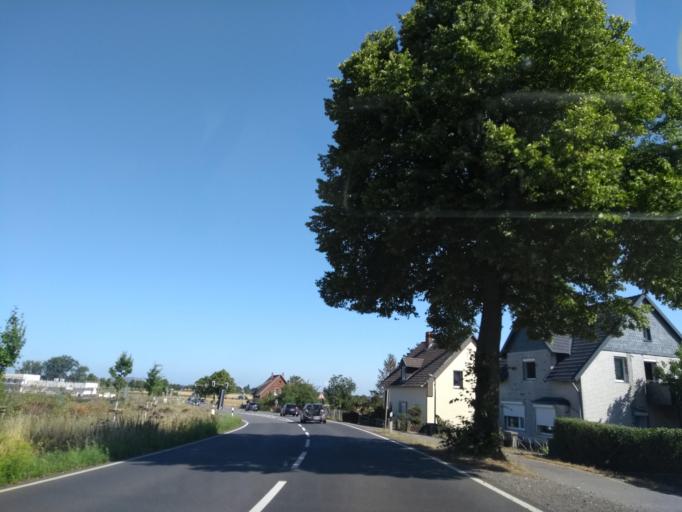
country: DE
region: Lower Saxony
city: Bad Nenndorf
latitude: 52.3421
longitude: 9.3897
